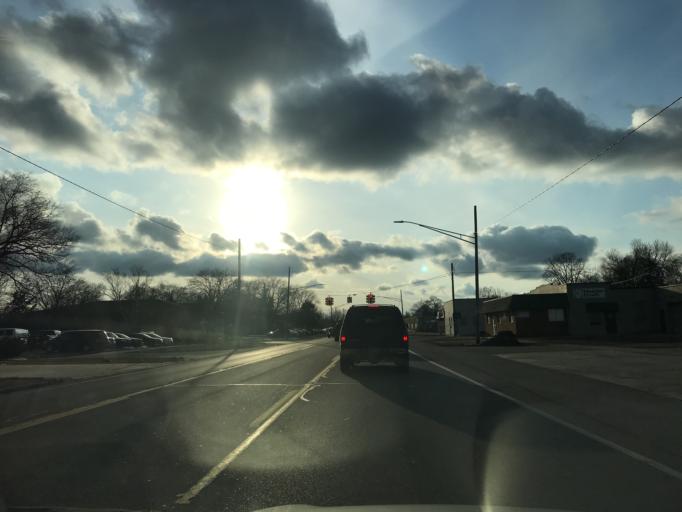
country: US
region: Michigan
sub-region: Wayne County
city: Redford
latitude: 42.4282
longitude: -83.3020
